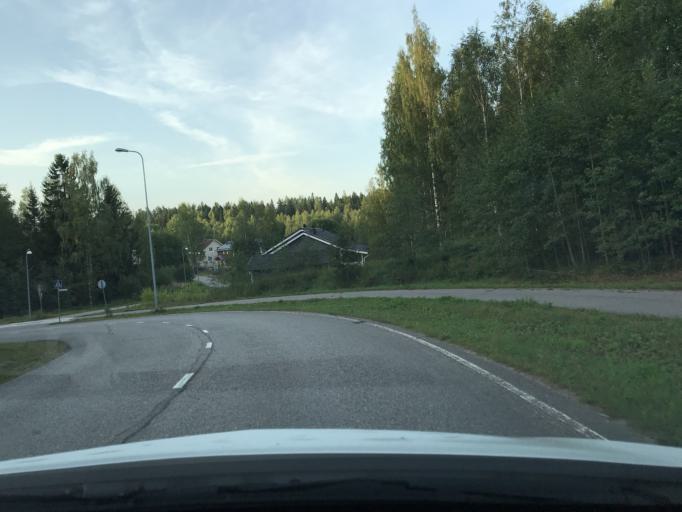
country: FI
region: Uusimaa
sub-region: Helsinki
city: Vihti
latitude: 60.4054
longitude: 24.4752
